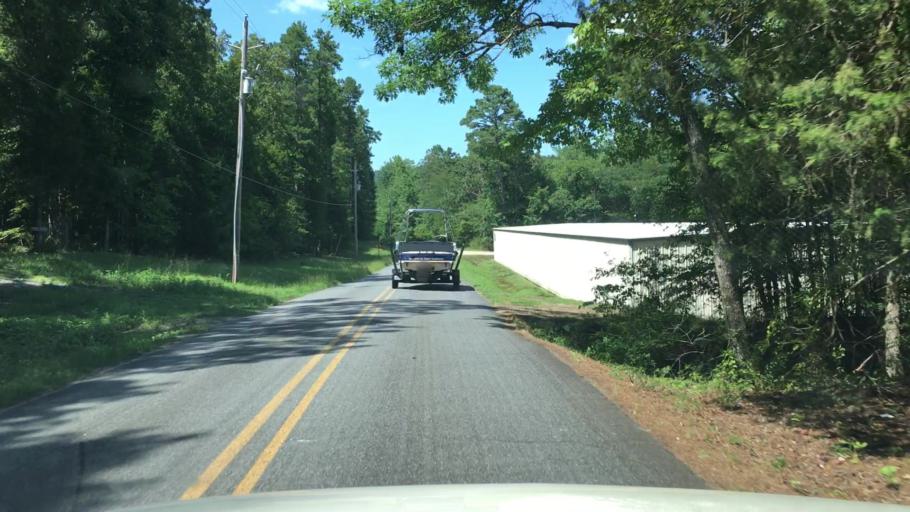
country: US
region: Arkansas
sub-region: Garland County
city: Rockwell
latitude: 34.5249
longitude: -93.3360
